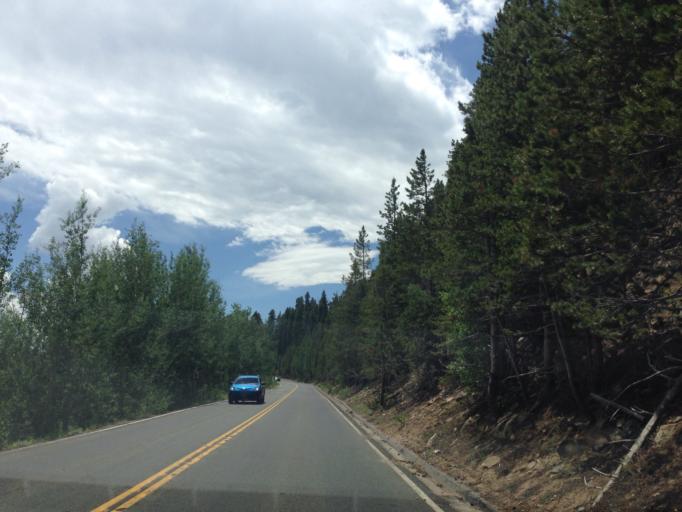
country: US
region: Colorado
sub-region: Larimer County
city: Estes Park
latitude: 40.3909
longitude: -105.6336
